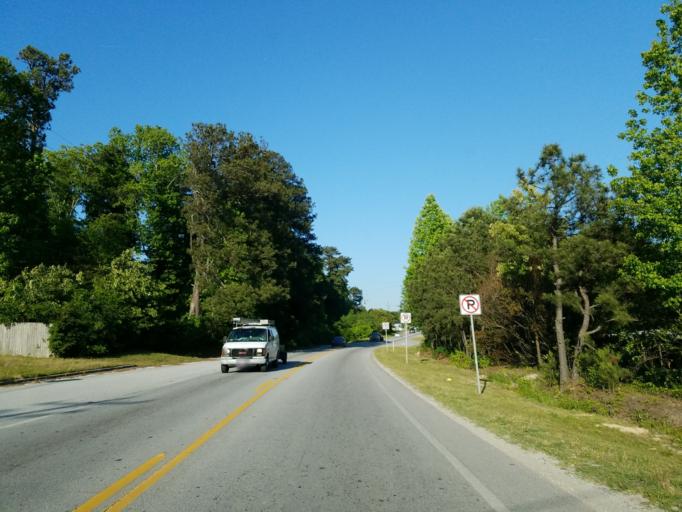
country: US
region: Georgia
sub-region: Douglas County
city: Lithia Springs
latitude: 33.7933
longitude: -84.6800
